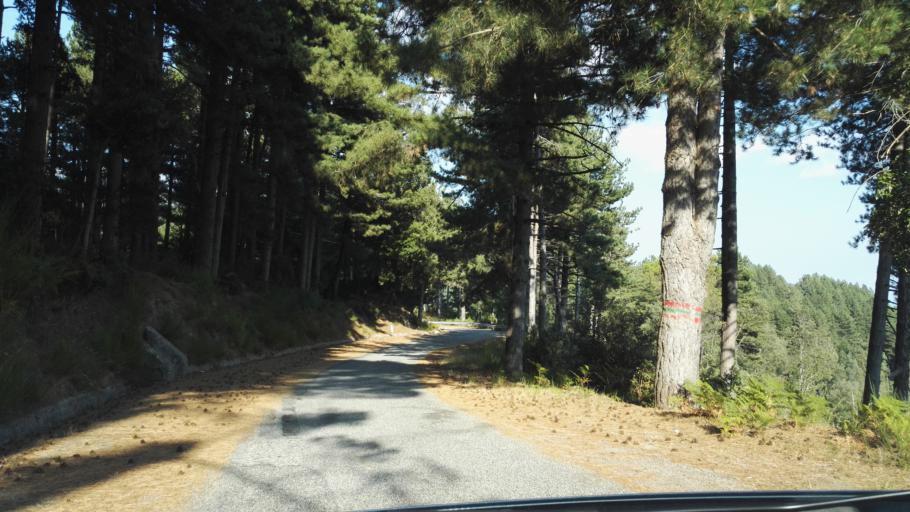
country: IT
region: Calabria
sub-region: Provincia di Vibo-Valentia
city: Nardodipace
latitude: 38.4623
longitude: 16.3531
